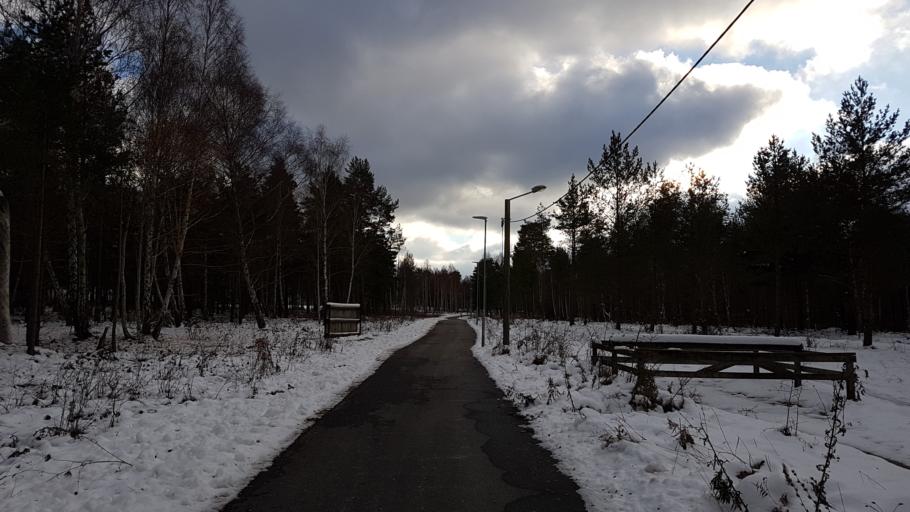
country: SE
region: Gotland
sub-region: Gotland
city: Vibble
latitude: 57.6094
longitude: 18.2805
